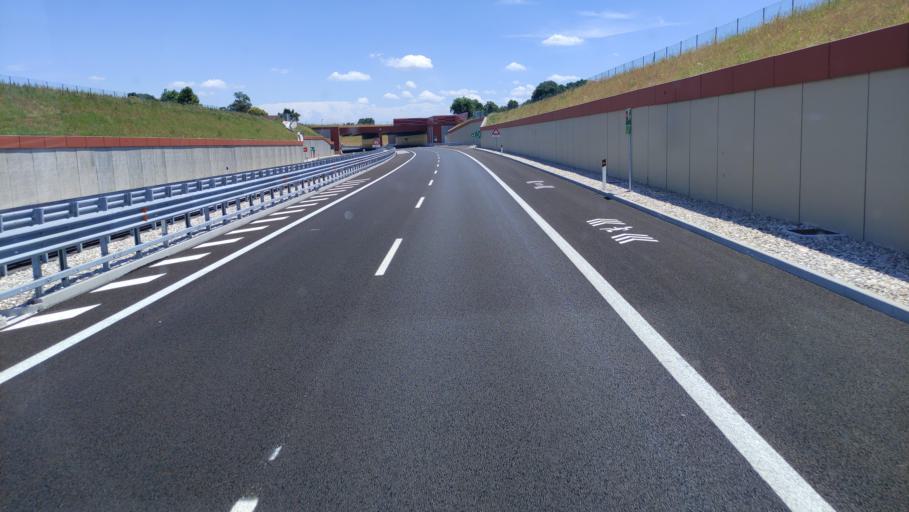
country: IT
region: Veneto
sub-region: Provincia di Treviso
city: Fanzolo
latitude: 45.7285
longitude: 11.9873
